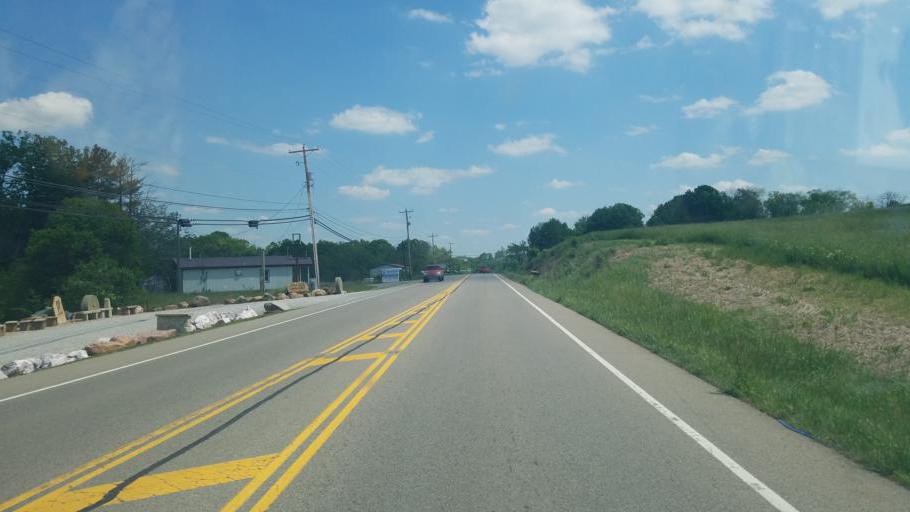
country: US
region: Ohio
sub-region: Muskingum County
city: Frazeysburg
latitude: 40.0285
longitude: -82.1021
